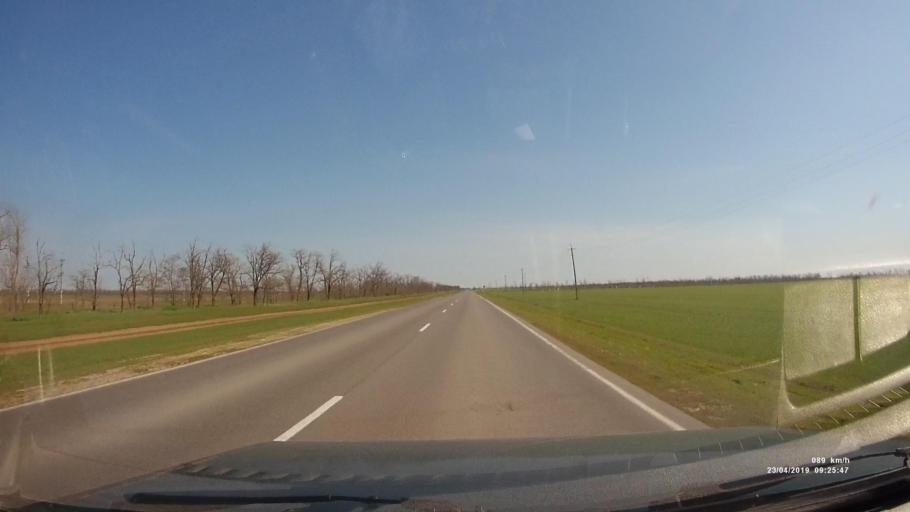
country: RU
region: Rostov
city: Proletarsk
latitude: 46.7199
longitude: 41.7663
